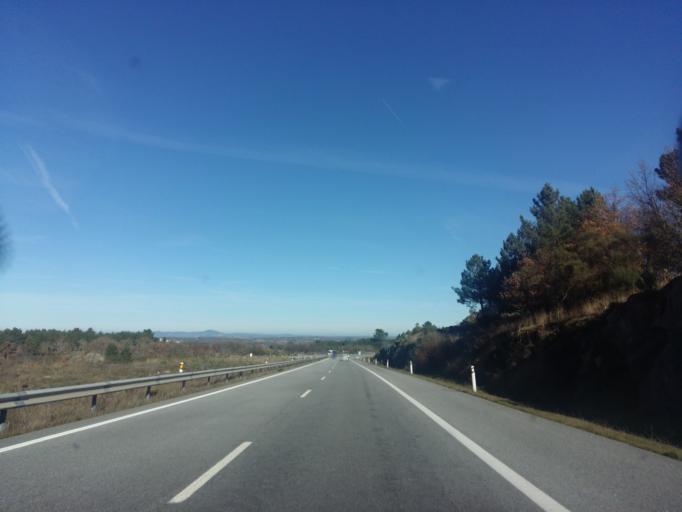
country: PT
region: Guarda
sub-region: Guarda
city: Sequeira
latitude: 40.5961
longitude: -7.1333
